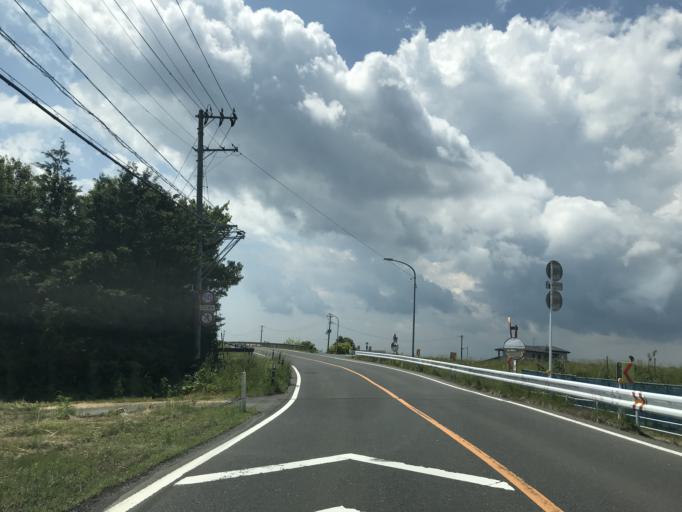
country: JP
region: Miyagi
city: Matsushima
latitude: 38.4601
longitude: 141.0872
